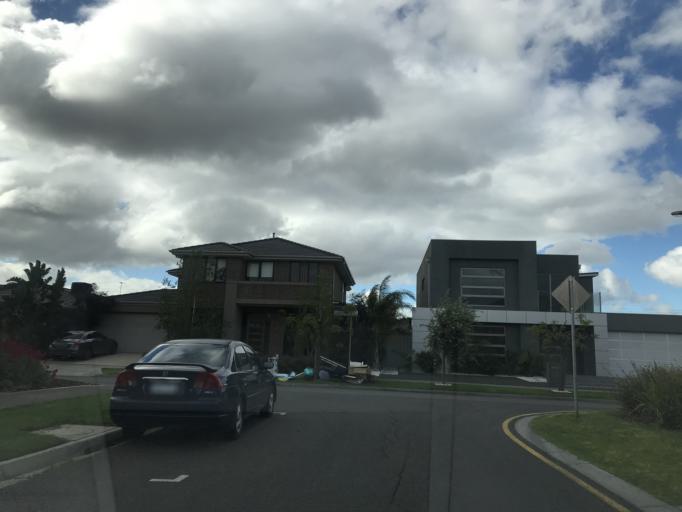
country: AU
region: Victoria
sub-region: Brimbank
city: Derrimut
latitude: -37.7931
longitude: 144.7931
